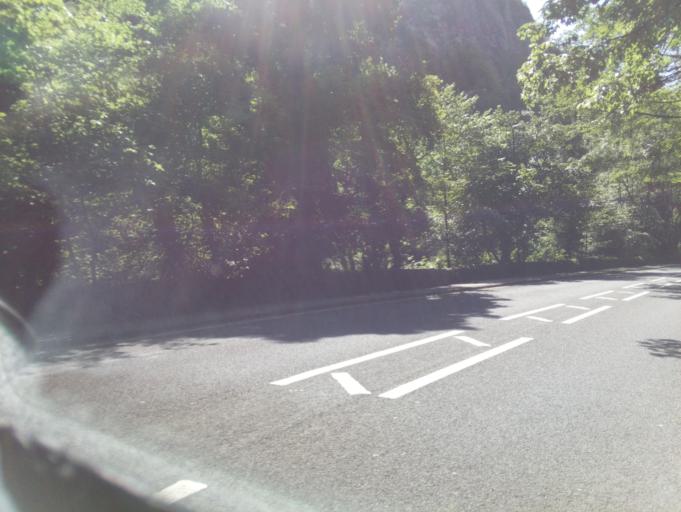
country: GB
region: England
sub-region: Derbyshire
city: Matlock
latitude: 53.1288
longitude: -1.5595
